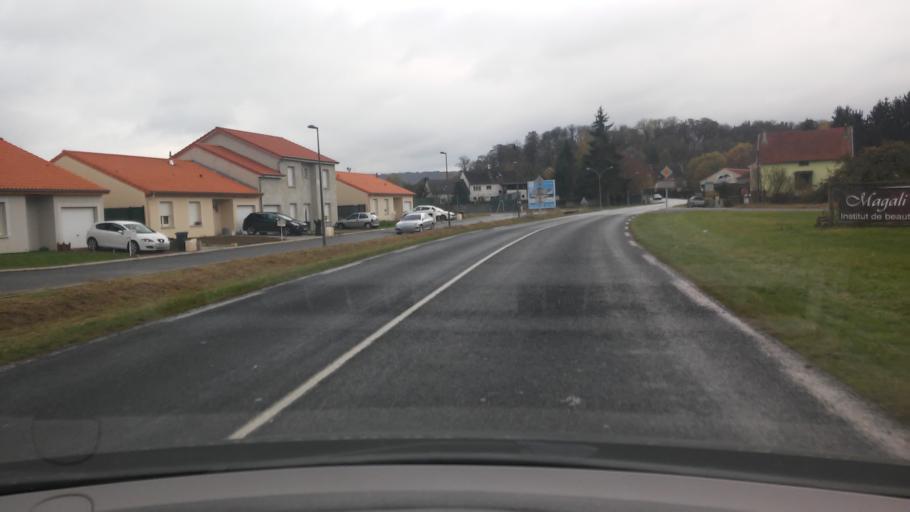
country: FR
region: Lorraine
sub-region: Departement de la Moselle
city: Kedange-sur-Canner
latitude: 49.2993
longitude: 6.3371
